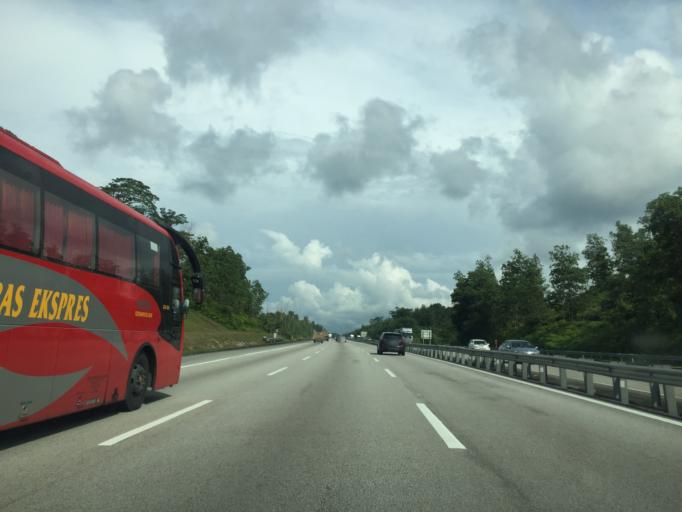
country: MY
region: Selangor
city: Serendah
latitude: 3.5147
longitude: 101.5278
